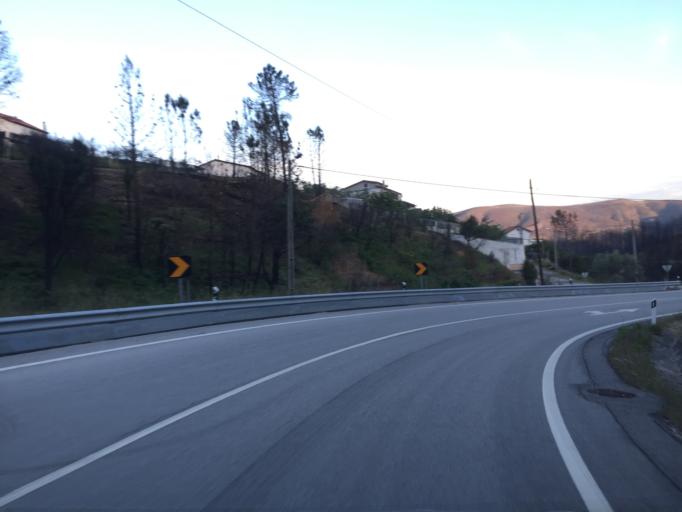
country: PT
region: Coimbra
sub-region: Pampilhosa da Serra
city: Pampilhosa da Serra
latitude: 40.0710
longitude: -7.9721
